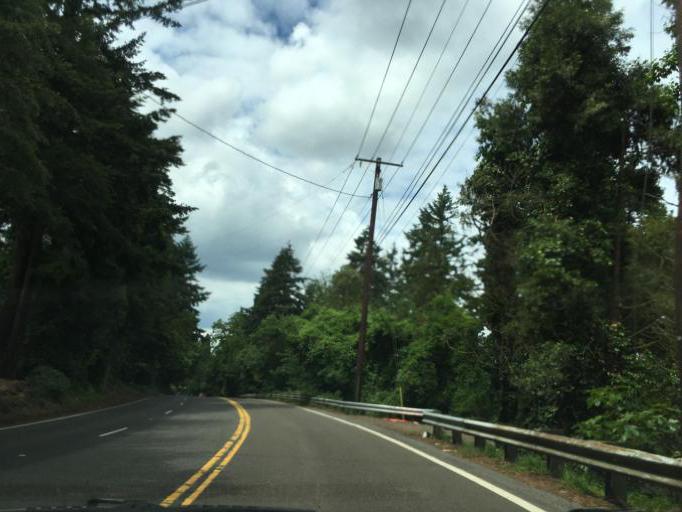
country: US
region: Oregon
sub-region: Clackamas County
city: Milwaukie
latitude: 45.4385
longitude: -122.6528
